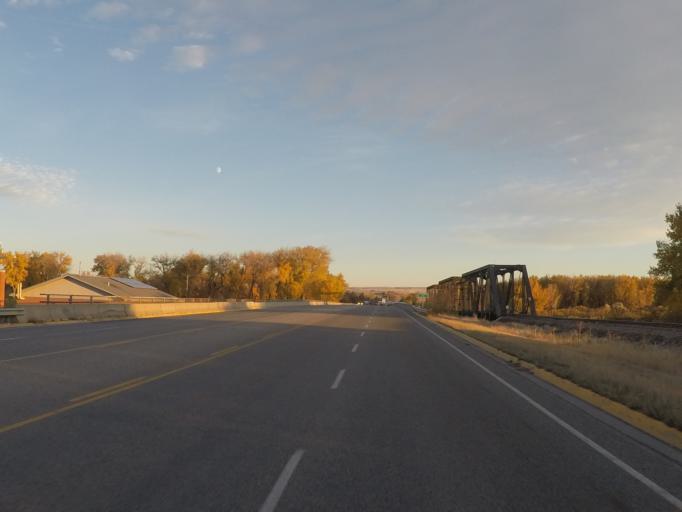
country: US
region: Montana
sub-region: Yellowstone County
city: Laurel
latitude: 45.6552
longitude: -108.7611
